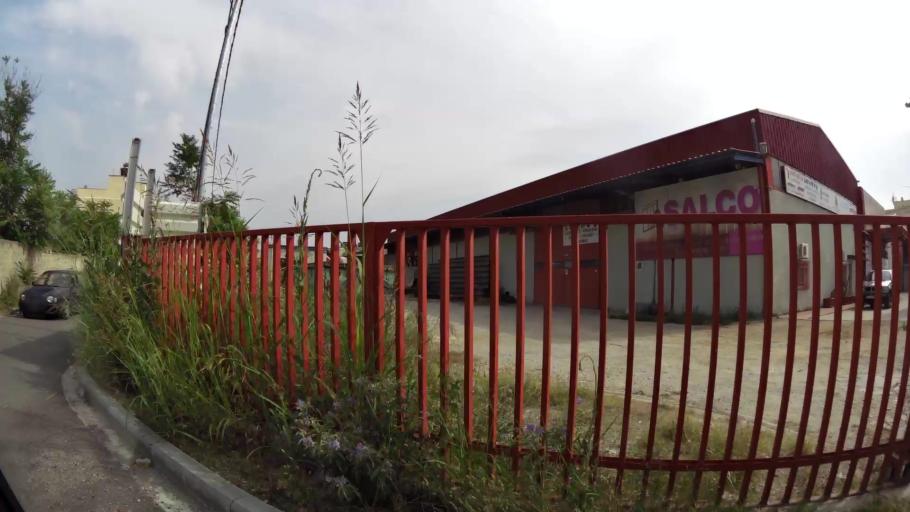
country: GR
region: Central Macedonia
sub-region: Nomos Thessalonikis
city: Stavroupoli
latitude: 40.6860
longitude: 22.9351
